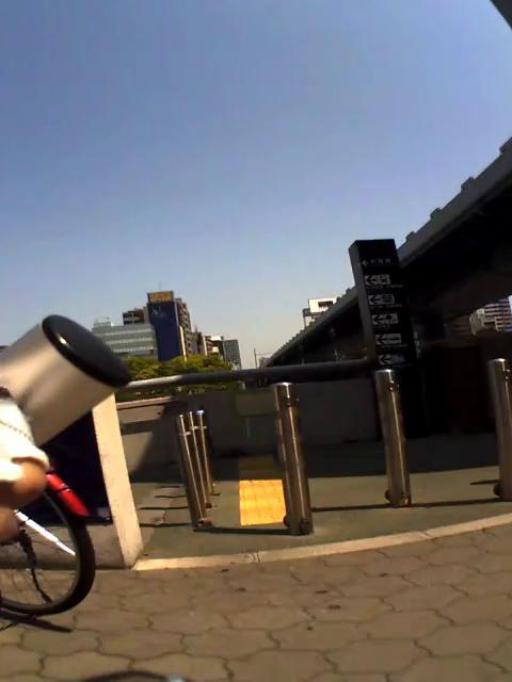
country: JP
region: Osaka
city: Osaka-shi
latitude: 34.6904
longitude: 135.5174
